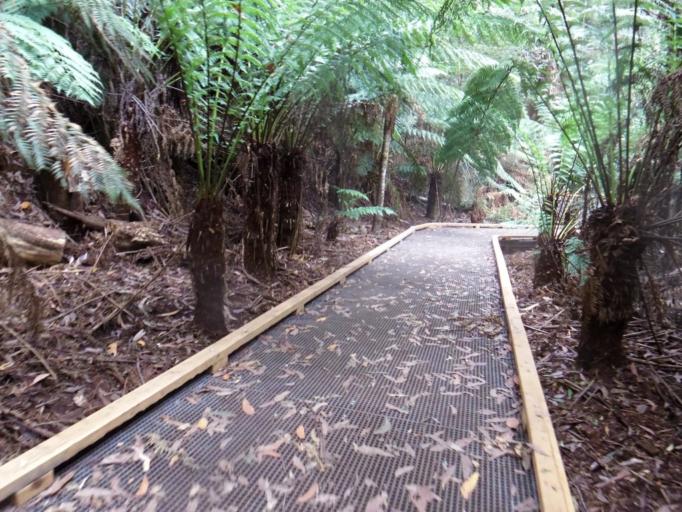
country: AU
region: Victoria
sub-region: Yarra Ranges
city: Healesville
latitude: -37.5272
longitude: 145.5224
